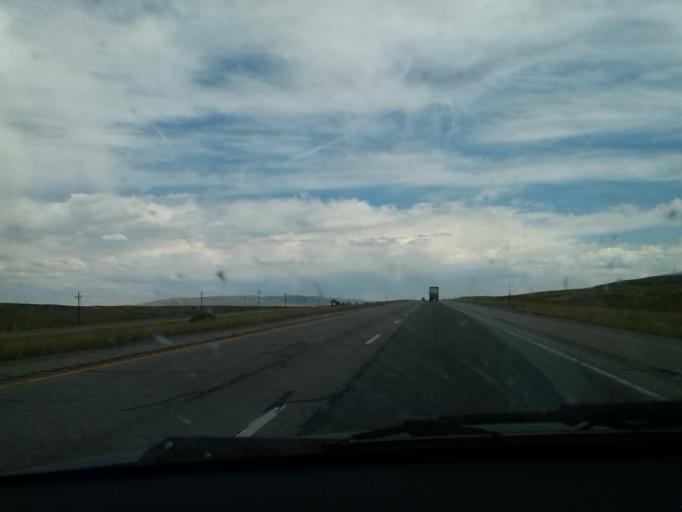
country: US
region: Wyoming
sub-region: Carbon County
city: Saratoga
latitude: 41.7430
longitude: -106.8792
